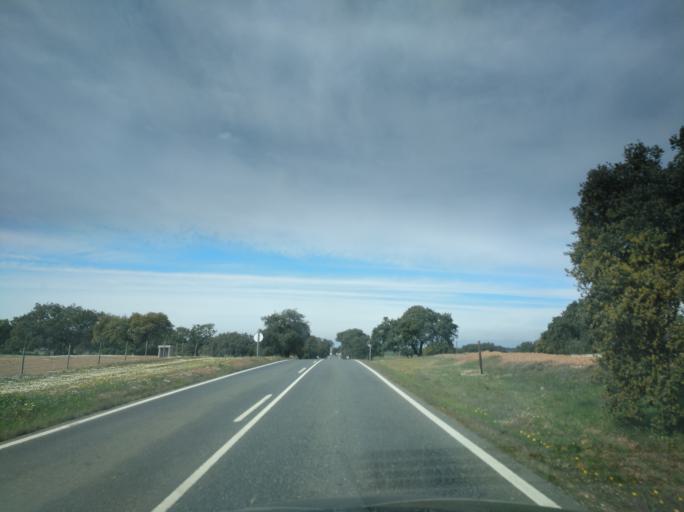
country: PT
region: Beja
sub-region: Mertola
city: Mertola
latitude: 37.7561
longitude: -7.8096
